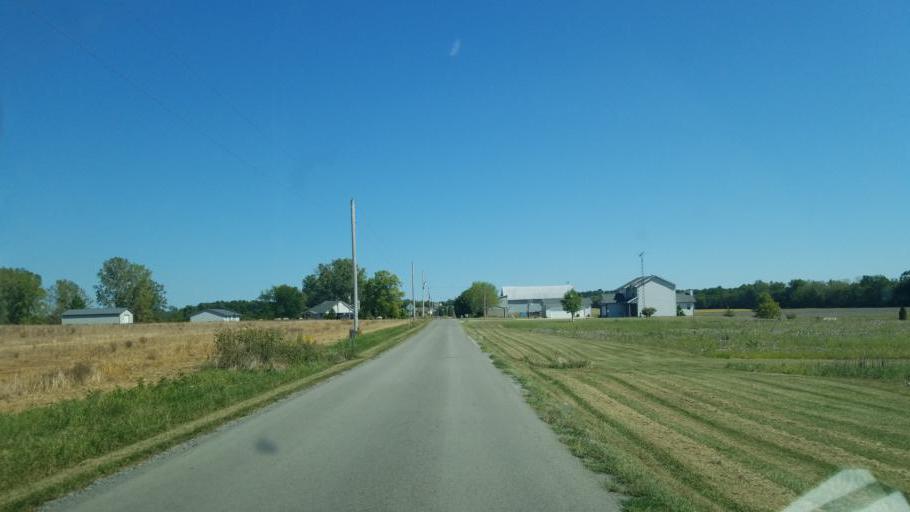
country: US
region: Ohio
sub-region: Logan County
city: Bellefontaine
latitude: 40.4245
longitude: -83.7967
